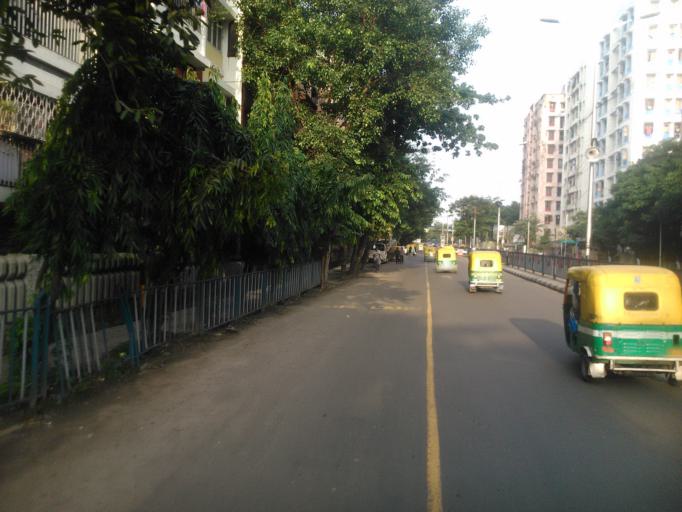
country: IN
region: West Bengal
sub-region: Kolkata
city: Kolkata
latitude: 22.5897
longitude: 88.3945
